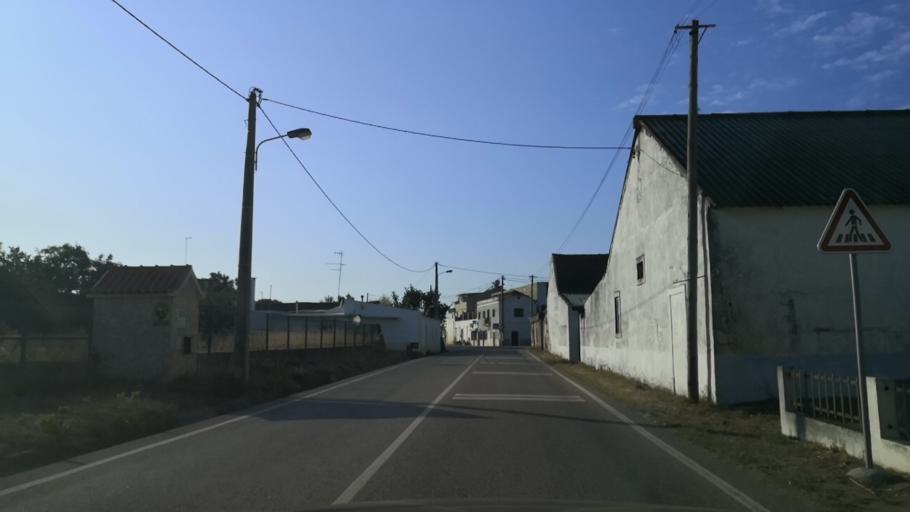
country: PT
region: Santarem
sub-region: Santarem
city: Santarem
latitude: 39.3356
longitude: -8.6622
